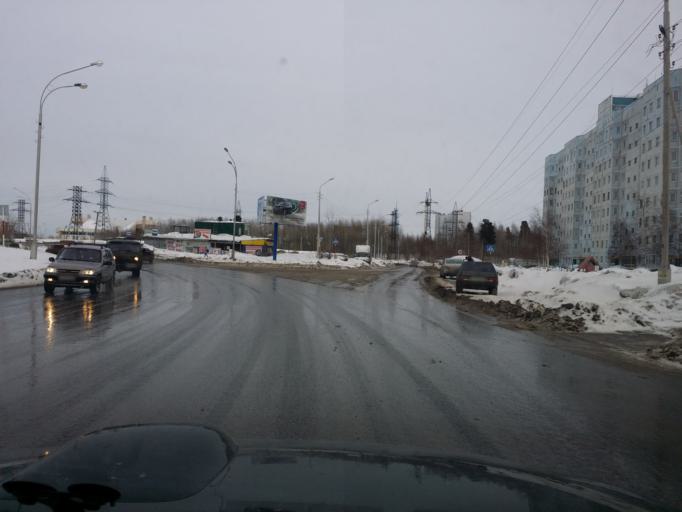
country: RU
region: Khanty-Mansiyskiy Avtonomnyy Okrug
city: Nizhnevartovsk
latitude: 60.9532
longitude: 76.5993
